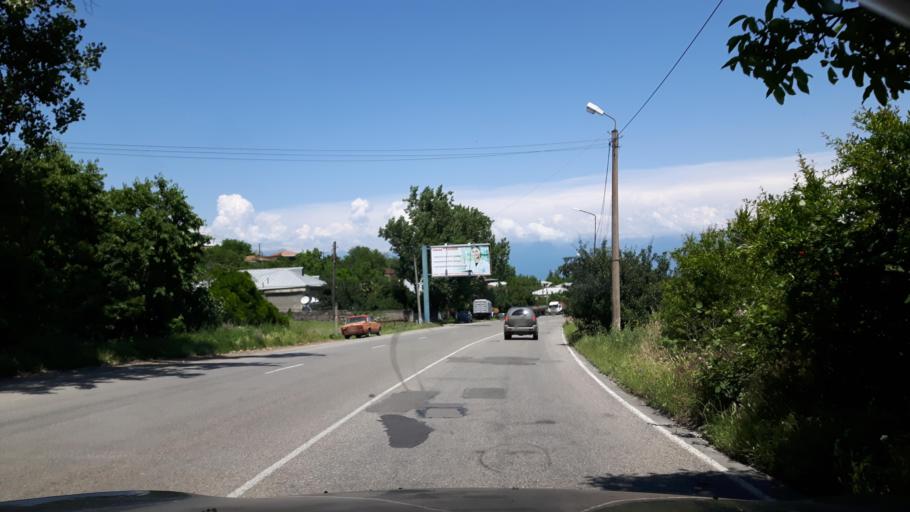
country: GE
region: Kakheti
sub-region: Gurjaani
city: Gurjaani
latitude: 41.6878
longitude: 45.8514
